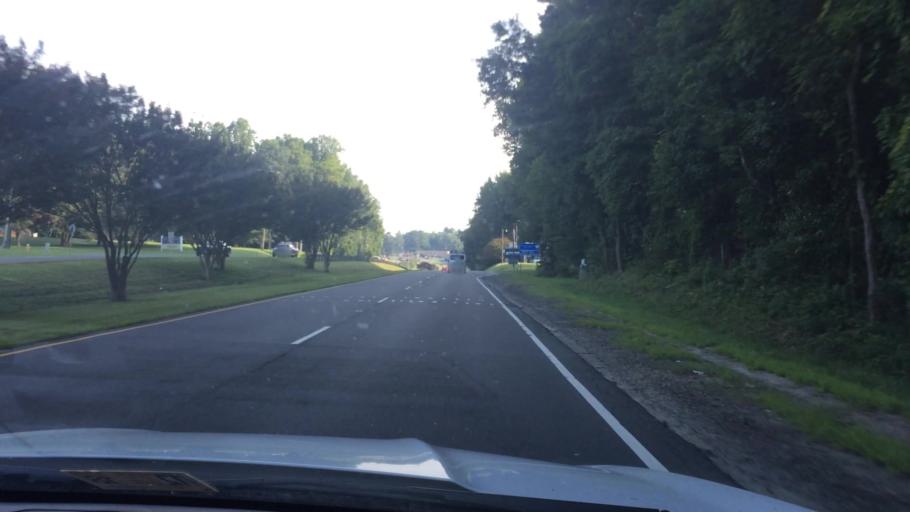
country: US
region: Virginia
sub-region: Gloucester County
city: Gloucester Courthouse
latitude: 37.4038
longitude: -76.5190
